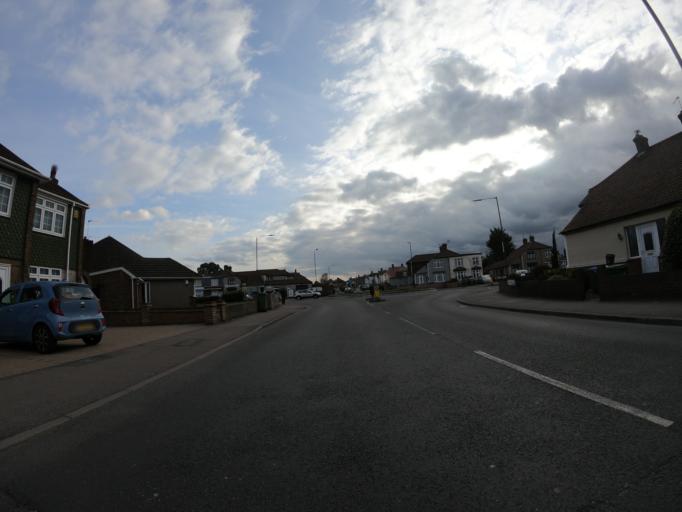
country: GB
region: England
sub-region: Greater London
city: Bexleyheath
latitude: 51.4682
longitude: 0.1425
